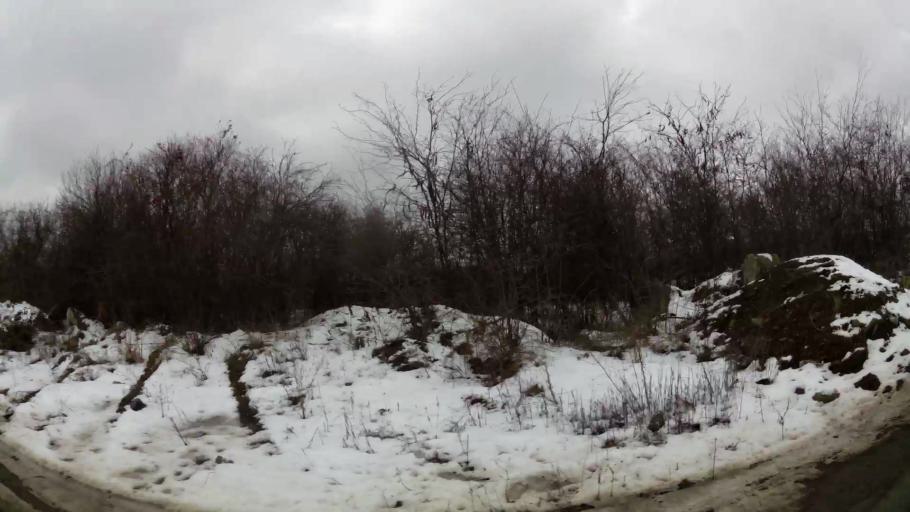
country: RO
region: Ilfov
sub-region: Comuna Mogosoaia
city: Mogosoaia
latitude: 44.5047
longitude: 26.0078
